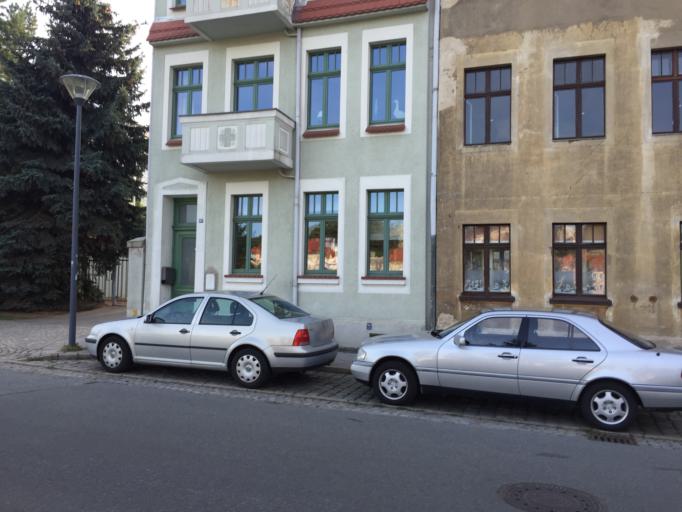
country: DE
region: Saxony
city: Goerlitz
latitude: 51.1549
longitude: 14.9961
